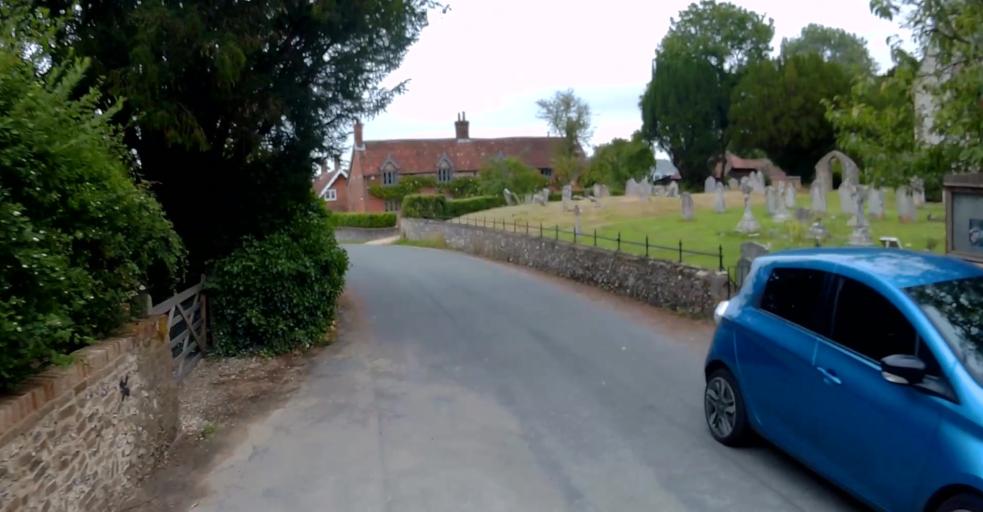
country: GB
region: England
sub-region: Hampshire
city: Kings Worthy
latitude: 51.0810
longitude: -1.2011
